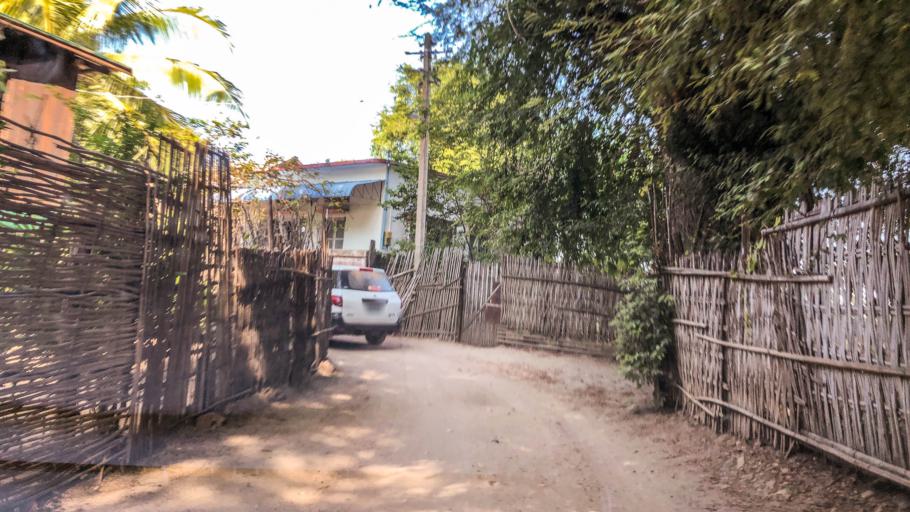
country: MM
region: Magway
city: Magway
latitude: 19.9770
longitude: 95.0335
